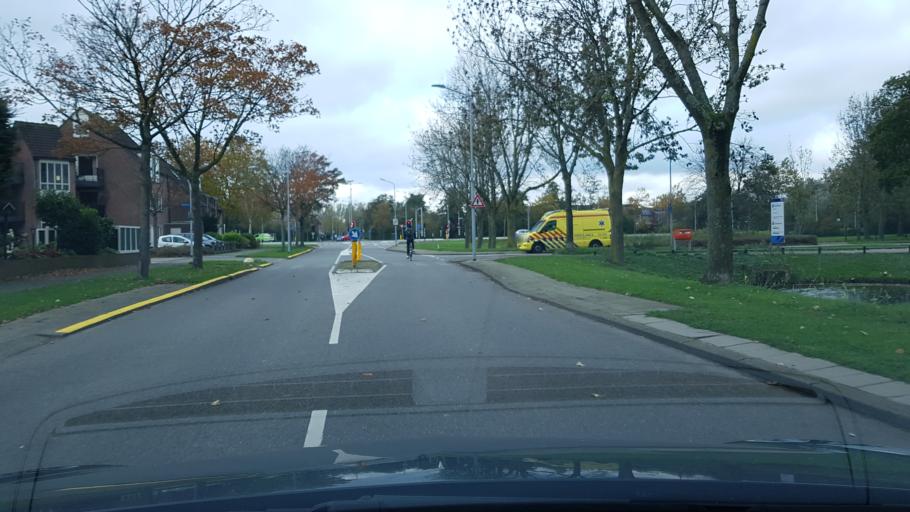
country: NL
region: North Holland
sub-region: Gemeente Haarlemmermeer
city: Hoofddorp
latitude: 52.3120
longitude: 4.6742
